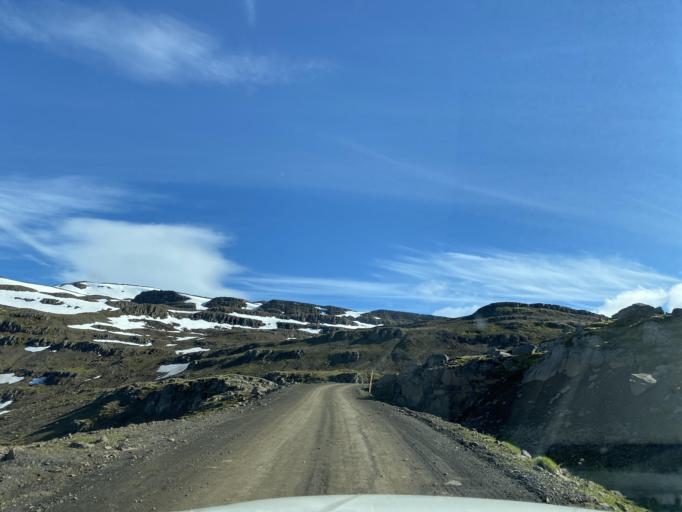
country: IS
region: East
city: Eskifjoerdur
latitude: 65.1685
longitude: -14.1289
